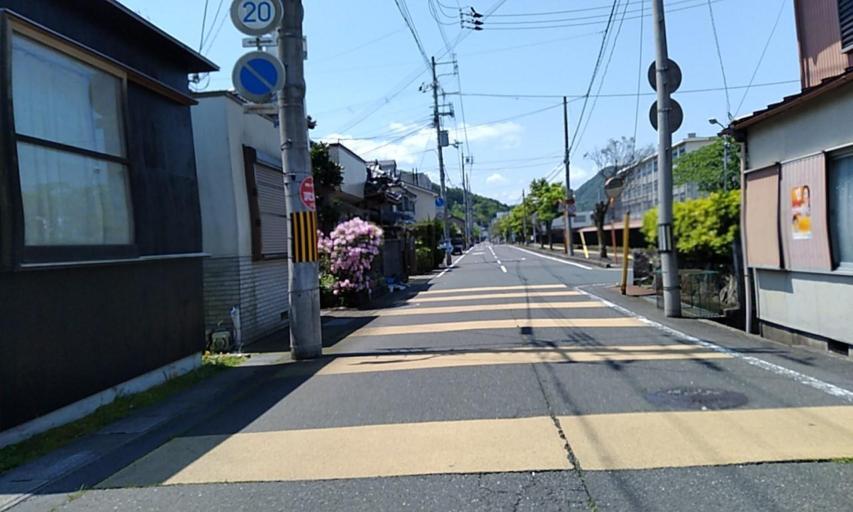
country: JP
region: Kyoto
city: Maizuru
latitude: 35.4479
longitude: 135.3328
